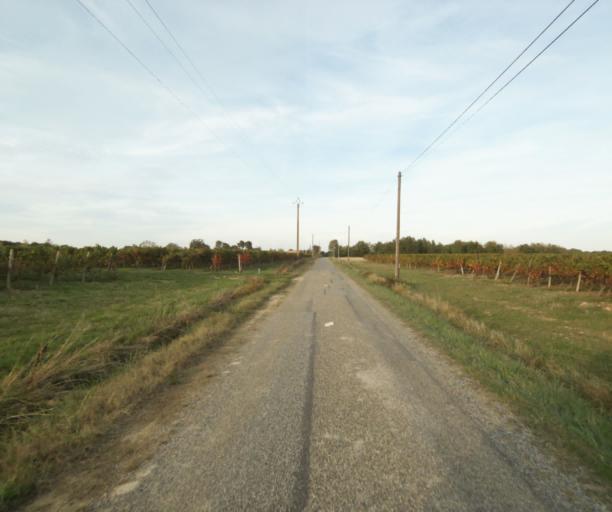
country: FR
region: Midi-Pyrenees
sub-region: Departement du Tarn-et-Garonne
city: Campsas
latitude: 43.8679
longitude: 1.3355
